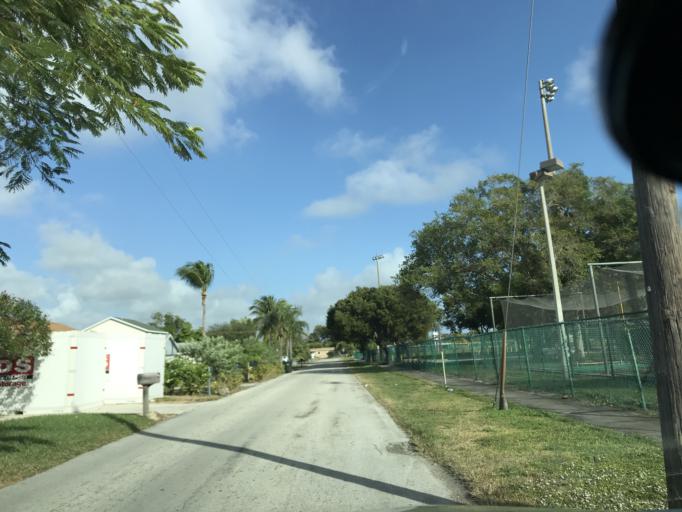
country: US
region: Florida
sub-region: Palm Beach County
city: Delray Beach
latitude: 26.4655
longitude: -80.0864
